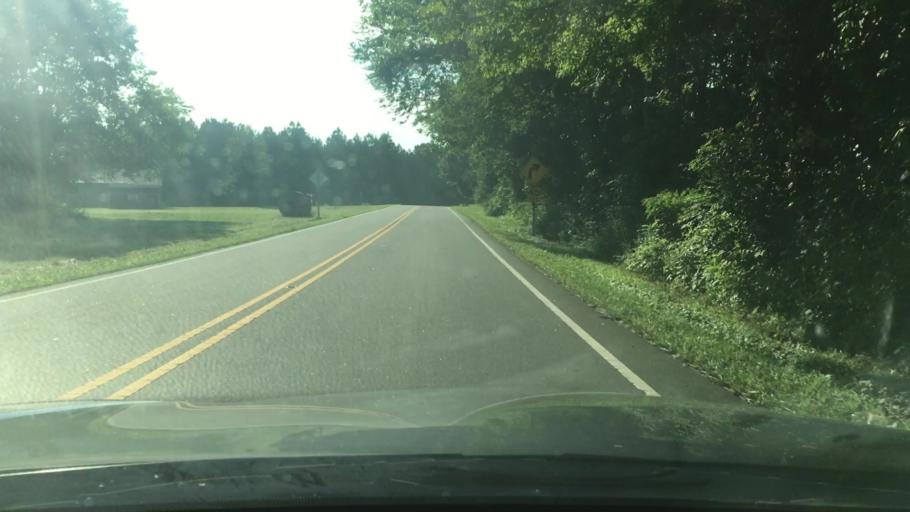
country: US
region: North Carolina
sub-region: Caswell County
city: Yanceyville
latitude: 36.2658
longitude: -79.3425
